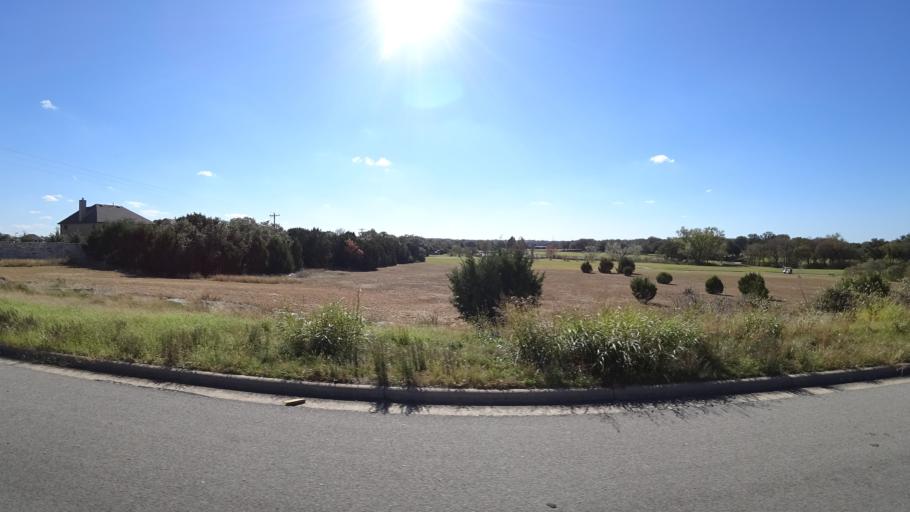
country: US
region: Texas
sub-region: Travis County
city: Shady Hollow
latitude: 30.1844
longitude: -97.9090
